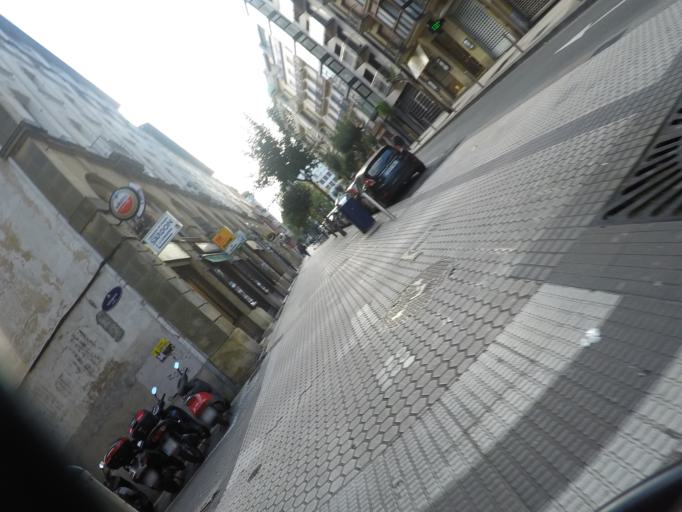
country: ES
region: Basque Country
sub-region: Provincia de Guipuzcoa
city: San Sebastian
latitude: 43.3143
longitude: -2.0011
